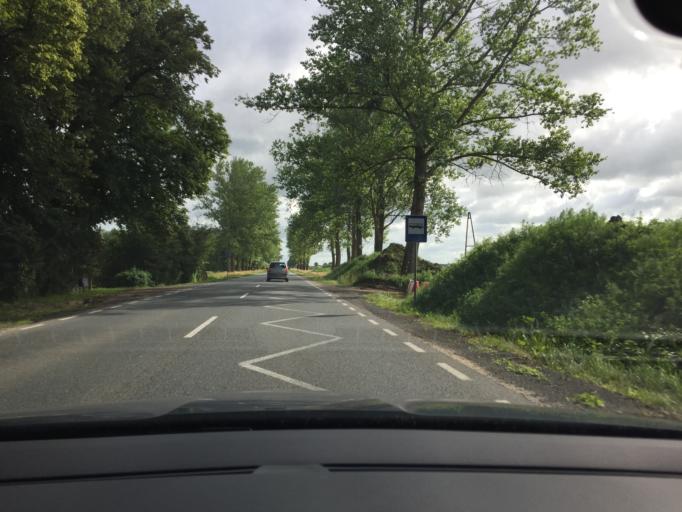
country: PL
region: West Pomeranian Voivodeship
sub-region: Powiat gryficki
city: Brojce
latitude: 53.8659
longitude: 15.3569
